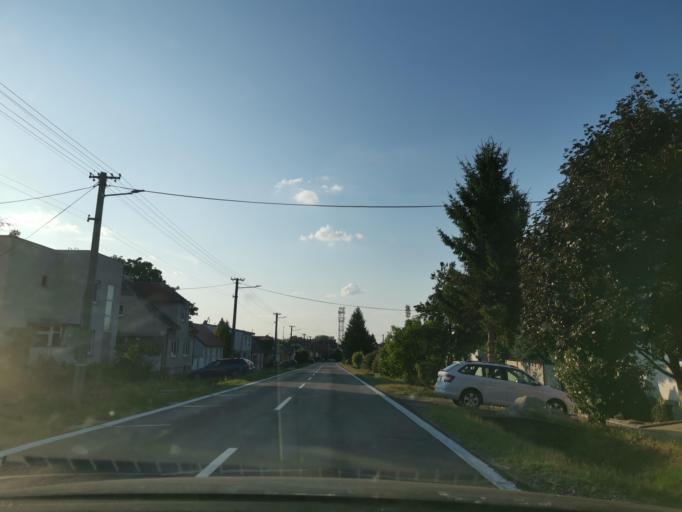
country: SK
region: Bratislavsky
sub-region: Okres Malacky
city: Malacky
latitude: 48.5064
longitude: 16.9990
